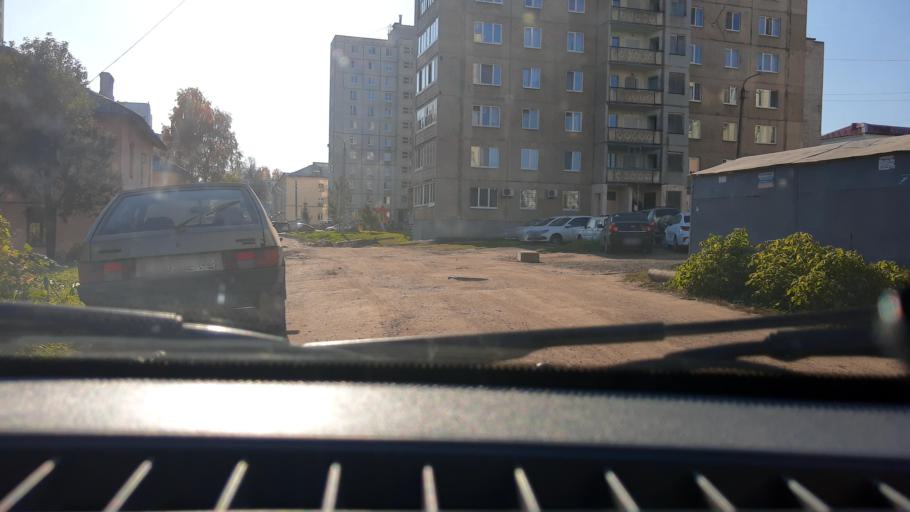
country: RU
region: Bashkortostan
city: Ufa
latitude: 54.7437
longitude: 55.9930
